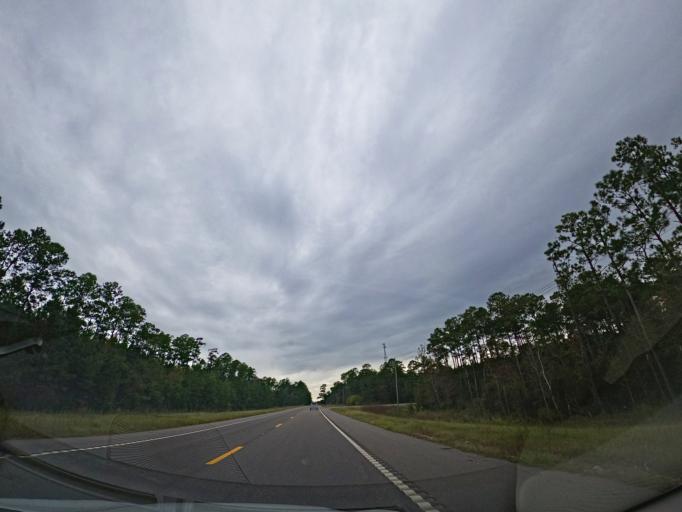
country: US
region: Mississippi
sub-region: Hancock County
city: Pearlington
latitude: 30.2498
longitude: -89.5919
